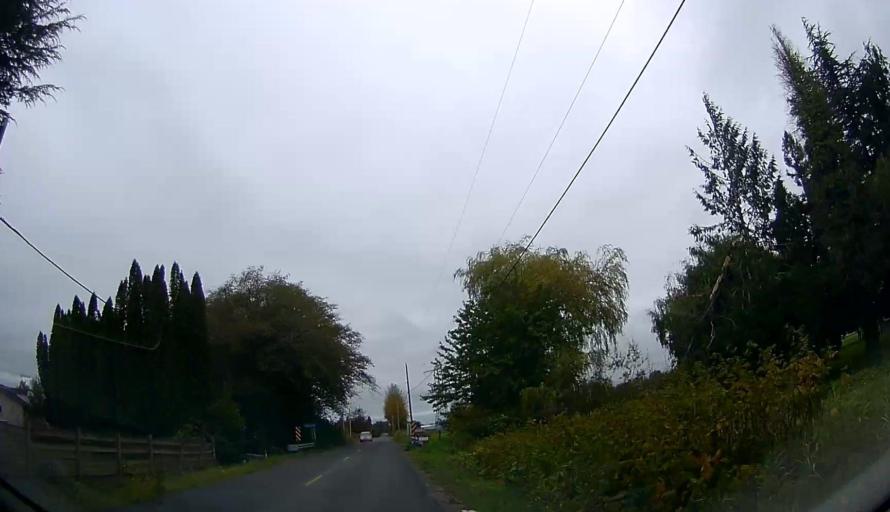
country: US
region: Washington
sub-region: Skagit County
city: Sedro-Woolley
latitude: 48.5145
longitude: -122.1631
